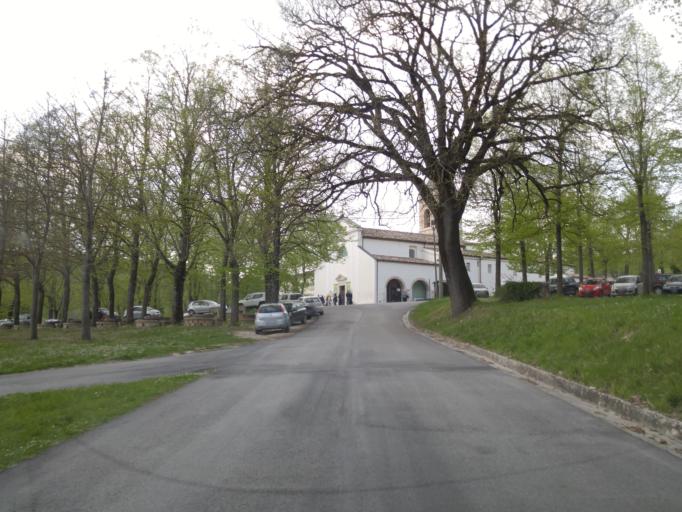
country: IT
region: The Marches
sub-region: Provincia di Pesaro e Urbino
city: Acqualagna
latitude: 43.6401
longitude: 12.6931
